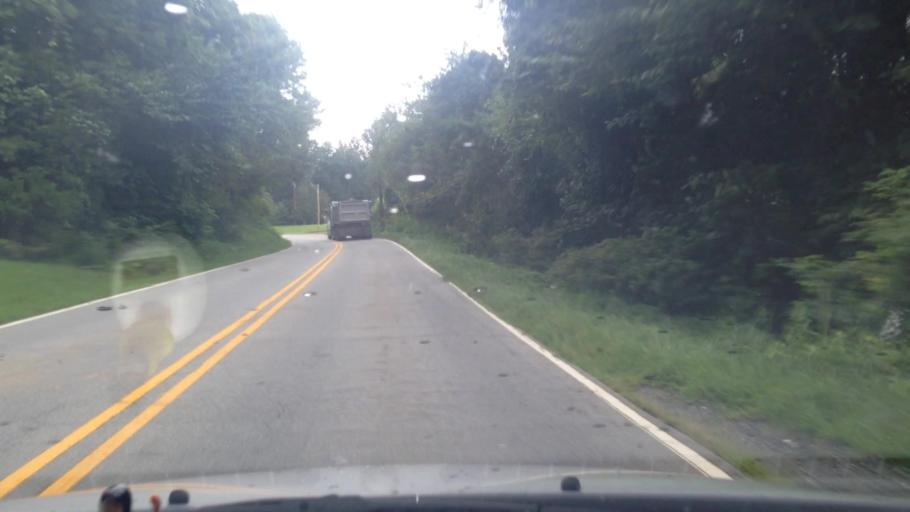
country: US
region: North Carolina
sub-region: Forsyth County
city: Walkertown
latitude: 36.1845
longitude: -80.1596
